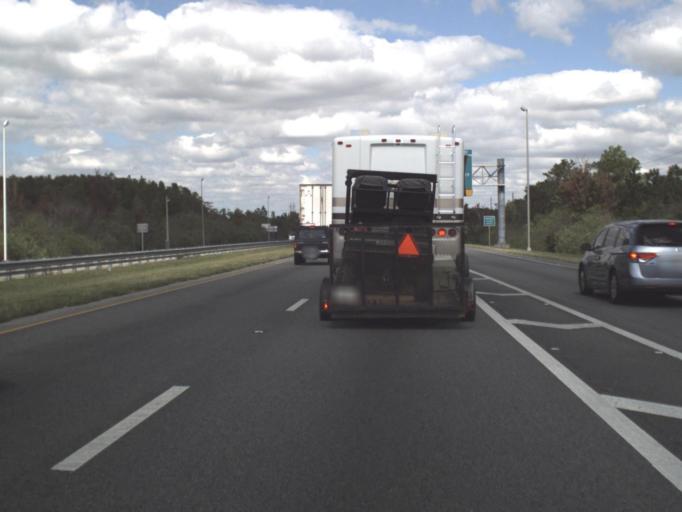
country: US
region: Florida
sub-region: Osceola County
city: Buenaventura Lakes
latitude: 28.3469
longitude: -81.3826
